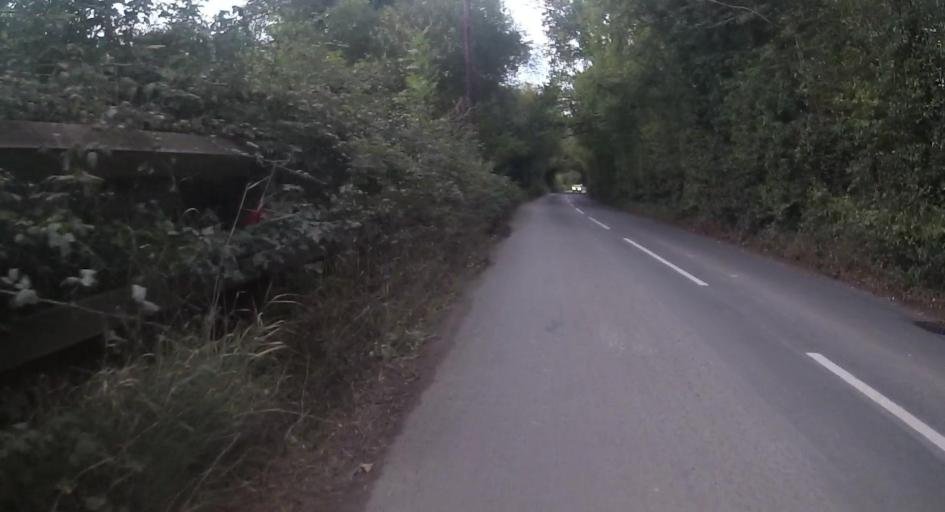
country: GB
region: England
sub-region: Hampshire
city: Fleet
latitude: 51.2479
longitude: -0.8612
